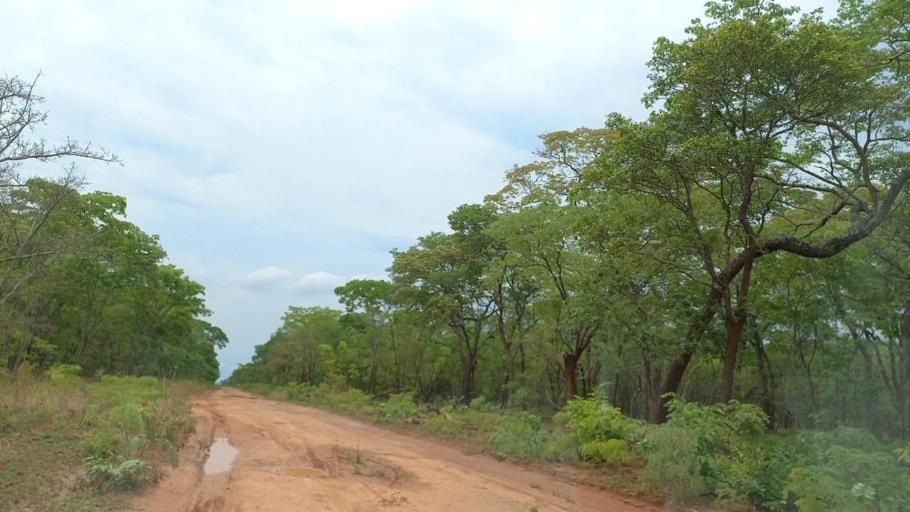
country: ZM
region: North-Western
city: Kalengwa
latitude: -13.6107
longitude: 24.9755
